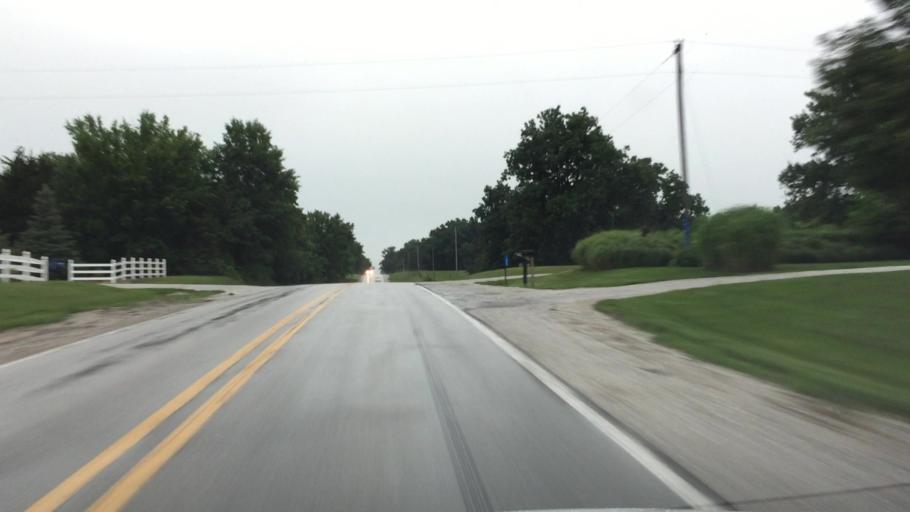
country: US
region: Illinois
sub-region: Hancock County
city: Carthage
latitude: 40.4344
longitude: -91.1401
